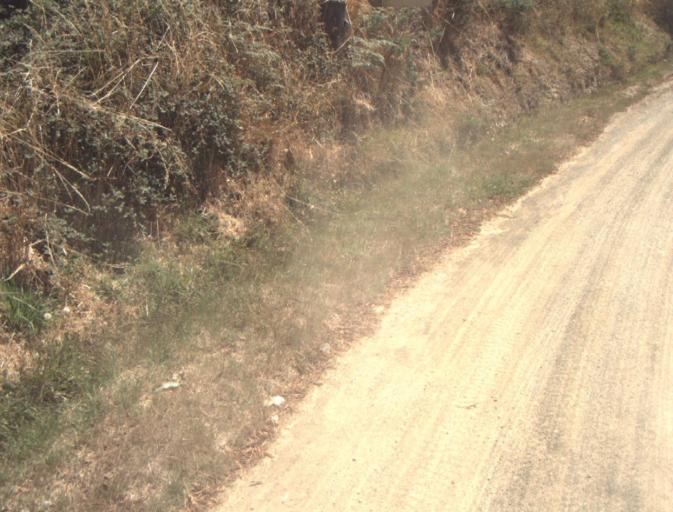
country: AU
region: Tasmania
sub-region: Launceston
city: Mayfield
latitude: -41.2704
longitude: 147.1328
